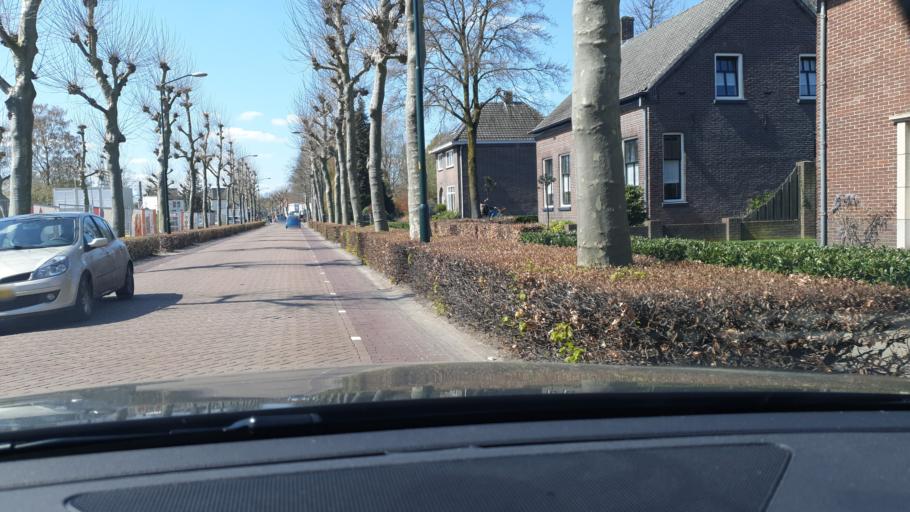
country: NL
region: North Brabant
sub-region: Gemeente Bladel en Netersel
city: Bladel
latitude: 51.3710
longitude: 5.2539
